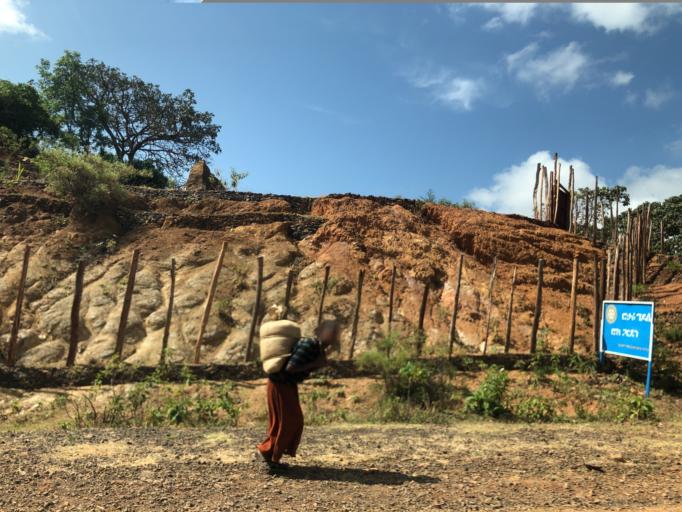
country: ET
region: Southern Nations, Nationalities, and People's Region
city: Gidole
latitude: 5.6418
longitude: 37.3836
